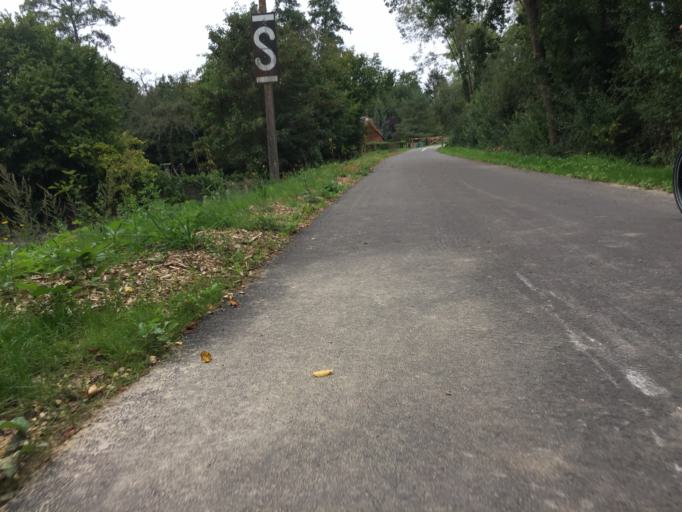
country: FR
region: Picardie
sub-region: Departement de l'Oise
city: Saint-Paul
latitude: 49.4027
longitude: 2.0093
